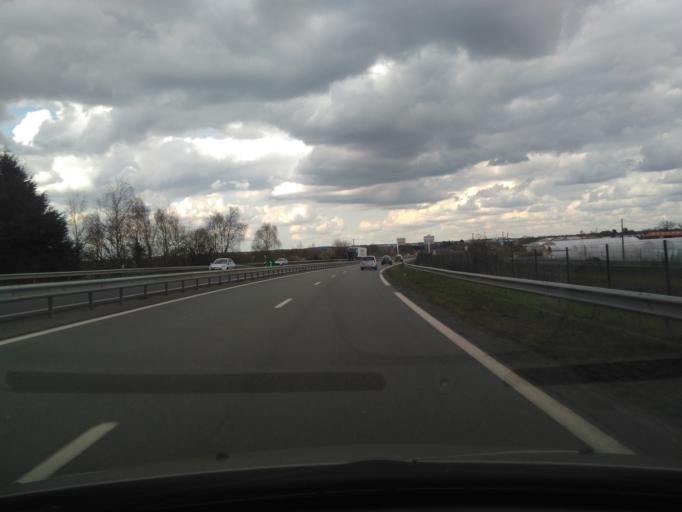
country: FR
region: Pays de la Loire
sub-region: Departement de la Vendee
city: Mortagne-sur-Sevre
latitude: 47.0029
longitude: -0.9398
